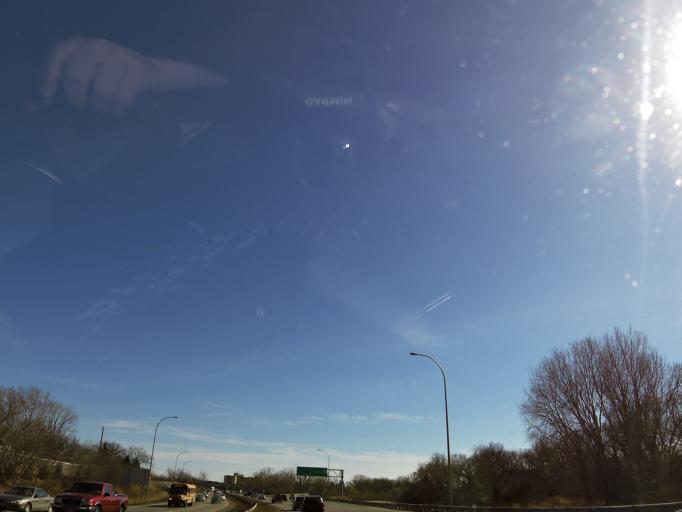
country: US
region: Minnesota
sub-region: Hennepin County
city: Minnetonka Mills
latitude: 44.9441
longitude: -93.4003
